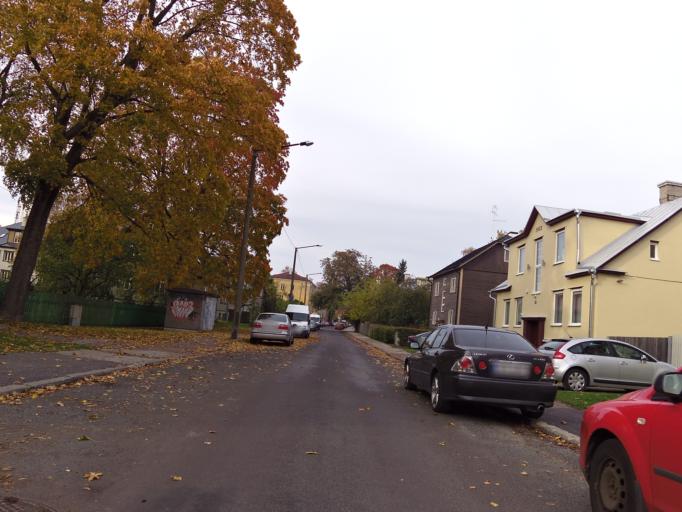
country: EE
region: Harju
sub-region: Tallinna linn
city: Tallinn
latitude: 59.4369
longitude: 24.7164
